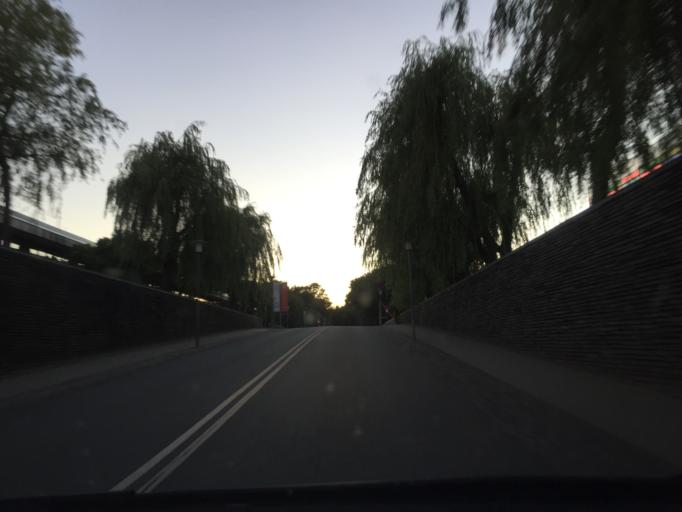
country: DK
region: Capital Region
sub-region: Lyngby-Tarbaek Kommune
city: Kongens Lyngby
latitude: 55.7805
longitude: 12.5179
